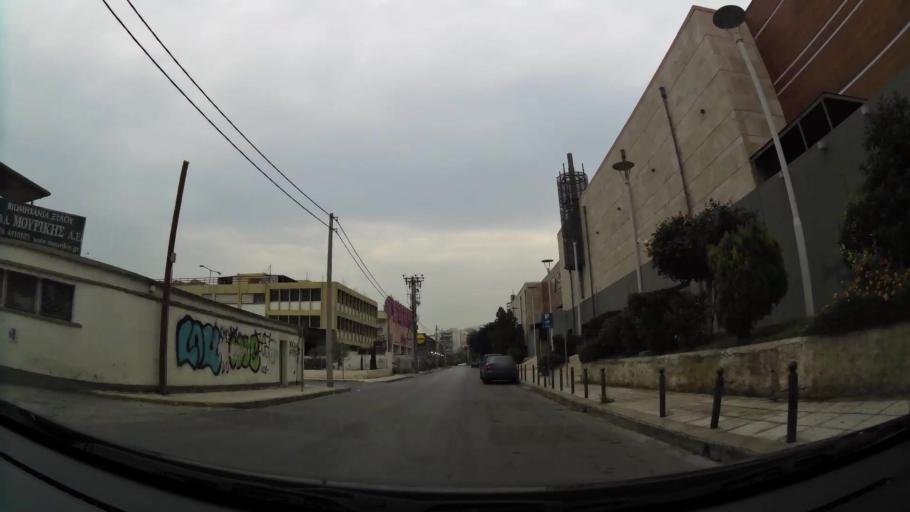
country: GR
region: Attica
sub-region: Nomos Piraios
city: Agios Ioannis Rentis
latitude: 37.9741
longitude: 23.6682
